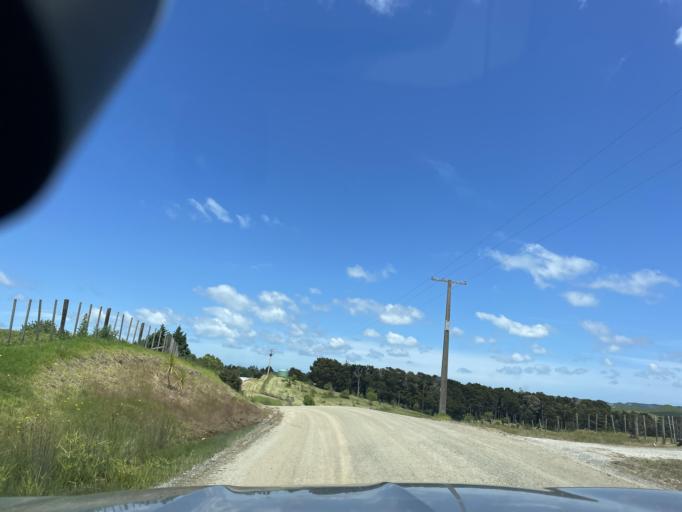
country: NZ
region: Auckland
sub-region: Auckland
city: Wellsford
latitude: -36.1719
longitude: 174.2734
